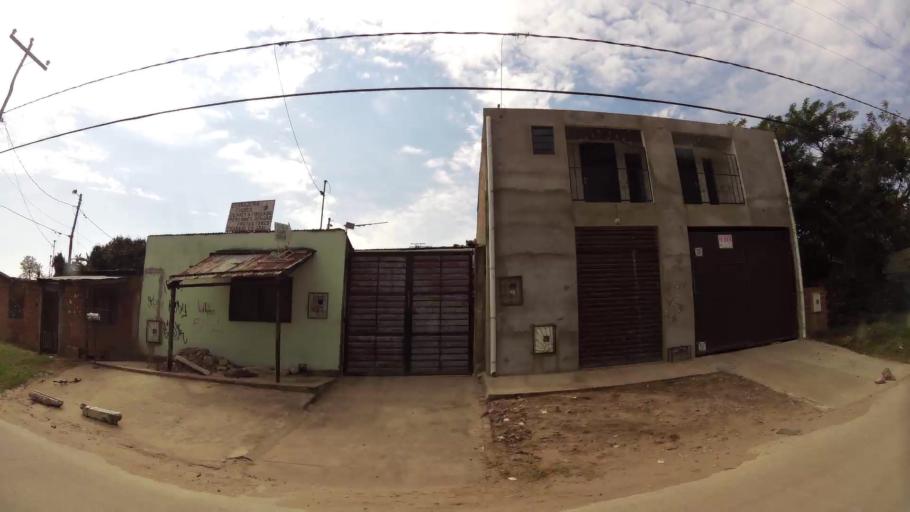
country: BO
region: Santa Cruz
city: Santa Cruz de la Sierra
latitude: -17.7329
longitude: -63.1818
